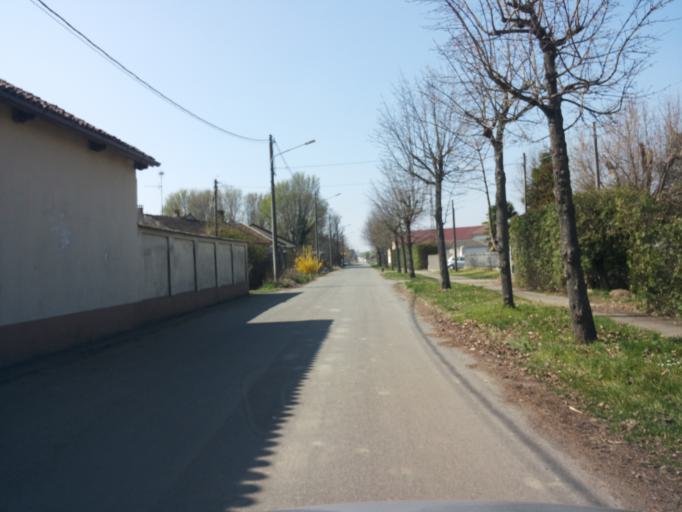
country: IT
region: Piedmont
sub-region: Provincia di Vercelli
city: Asigliano Vercellese
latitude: 45.2660
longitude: 8.4196
